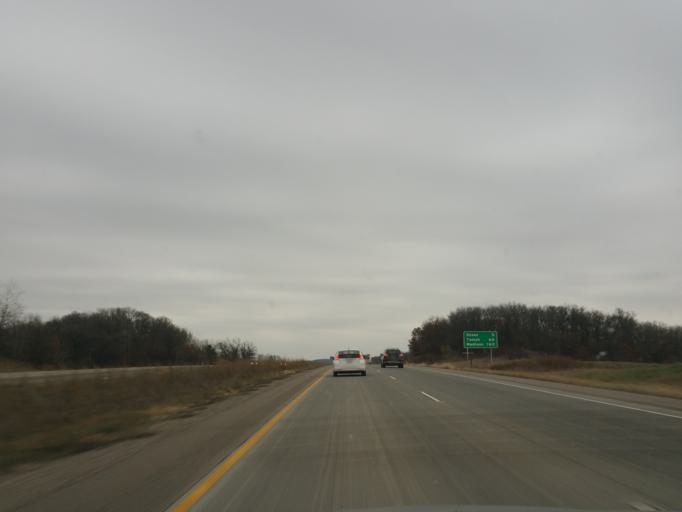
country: US
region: Wisconsin
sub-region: Trempealeau County
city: Osseo
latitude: 44.6320
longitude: -91.2905
